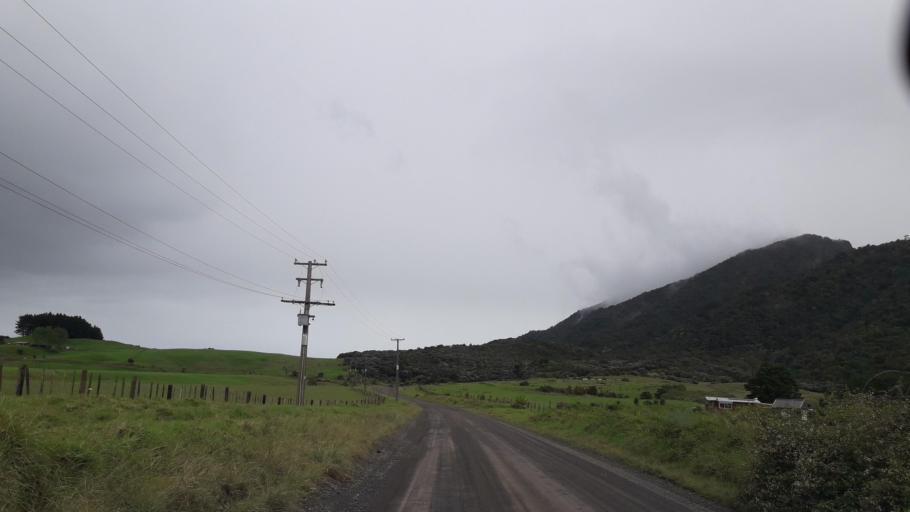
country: NZ
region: Northland
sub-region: Far North District
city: Kaitaia
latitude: -35.4044
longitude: 173.3679
